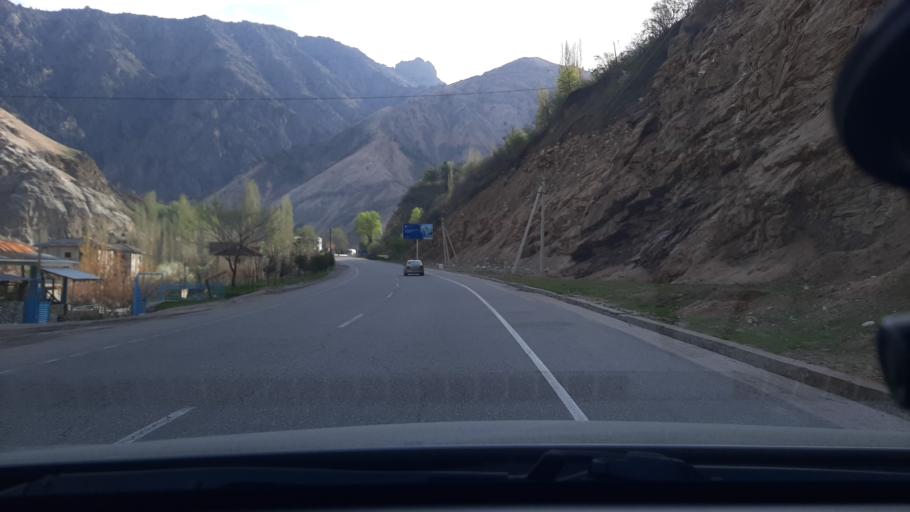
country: TJ
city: Tagob
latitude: 38.8451
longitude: 68.8428
